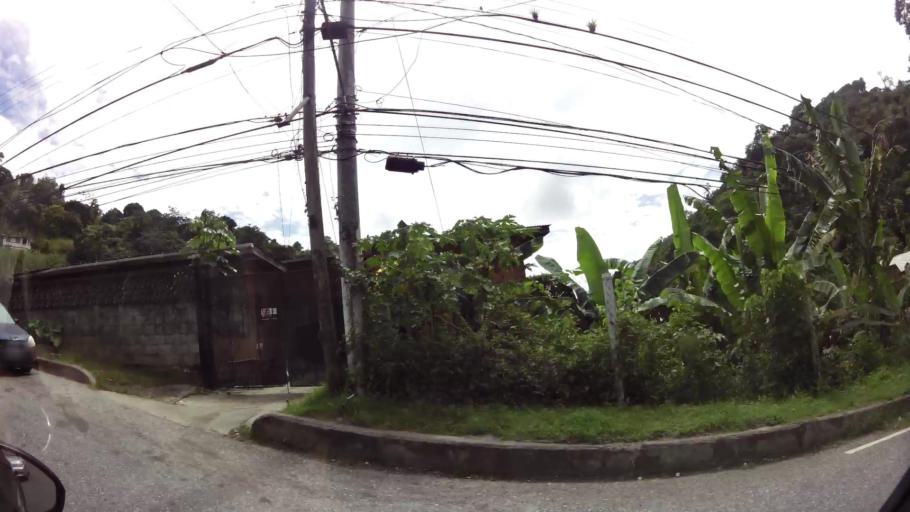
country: TT
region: Diego Martin
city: Petit Valley
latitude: 10.7148
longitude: -61.5249
